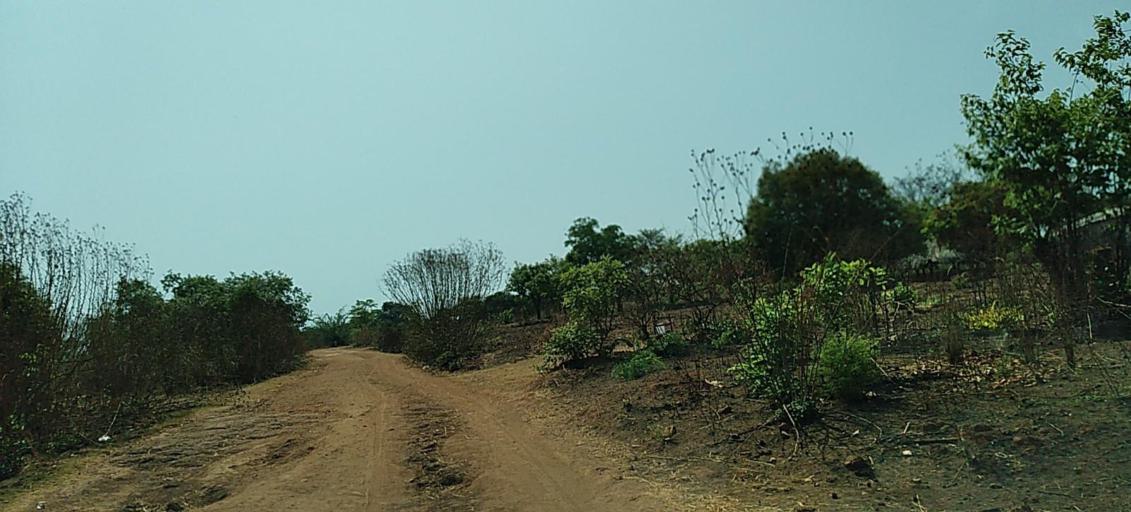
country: ZM
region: Copperbelt
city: Luanshya
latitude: -13.3486
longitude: 28.3988
